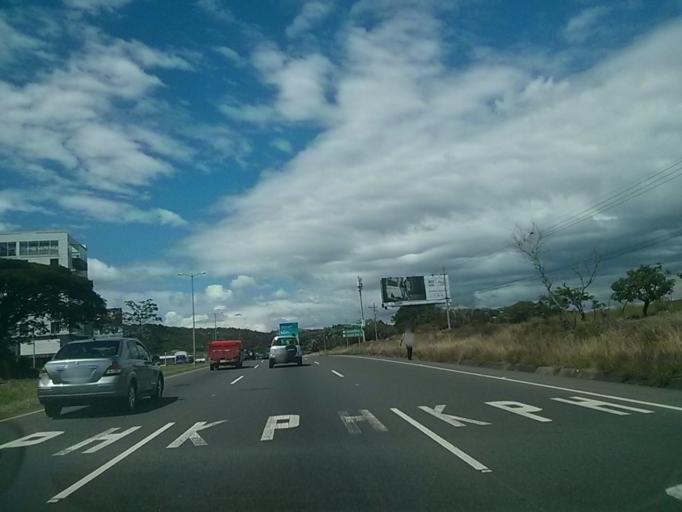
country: CR
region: San Jose
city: San Rafael
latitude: 9.9477
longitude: -84.1545
